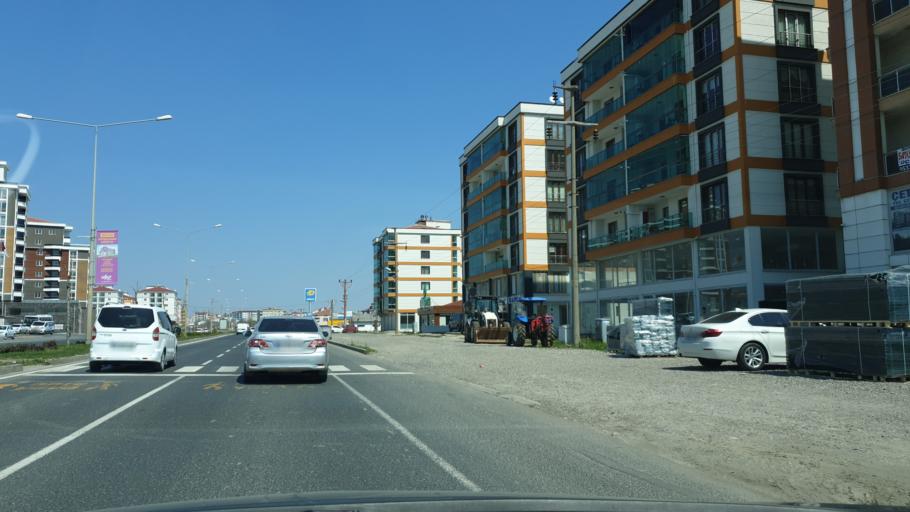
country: TR
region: Tekirdag
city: Corlu
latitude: 41.1535
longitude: 27.7801
